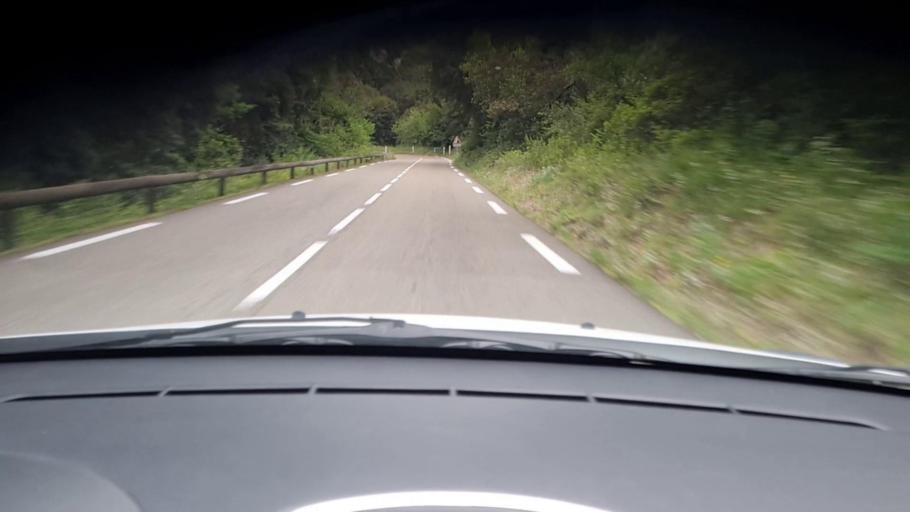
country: FR
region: Languedoc-Roussillon
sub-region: Departement du Gard
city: Blauzac
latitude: 43.9406
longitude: 4.3820
